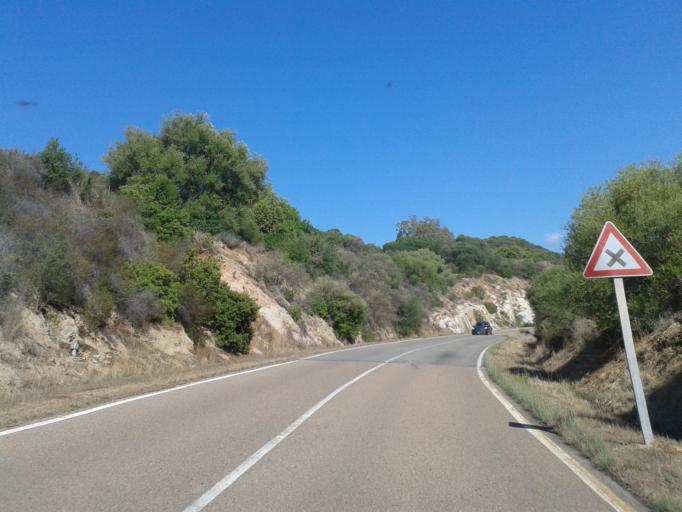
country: IT
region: Sardinia
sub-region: Provincia di Cagliari
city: Castiadas
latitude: 39.2230
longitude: 9.5590
